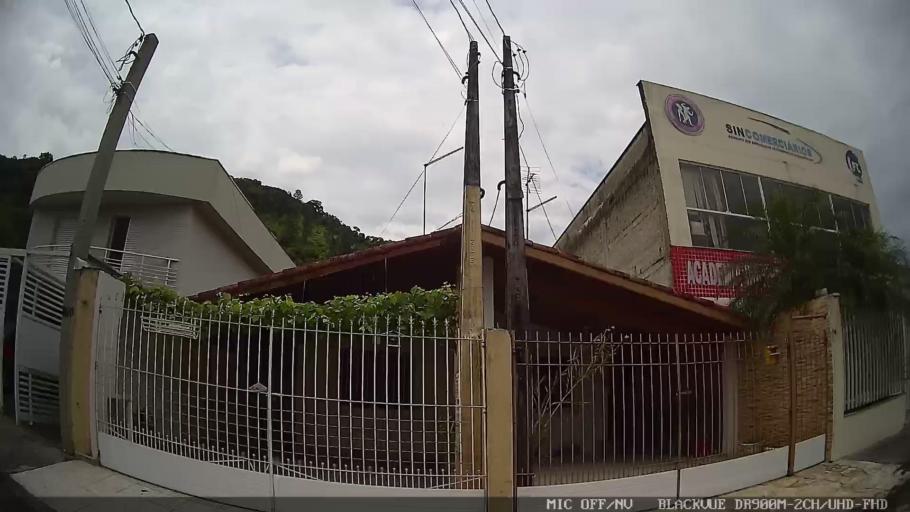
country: BR
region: Sao Paulo
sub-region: Caraguatatuba
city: Caraguatatuba
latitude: -23.6174
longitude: -45.4154
